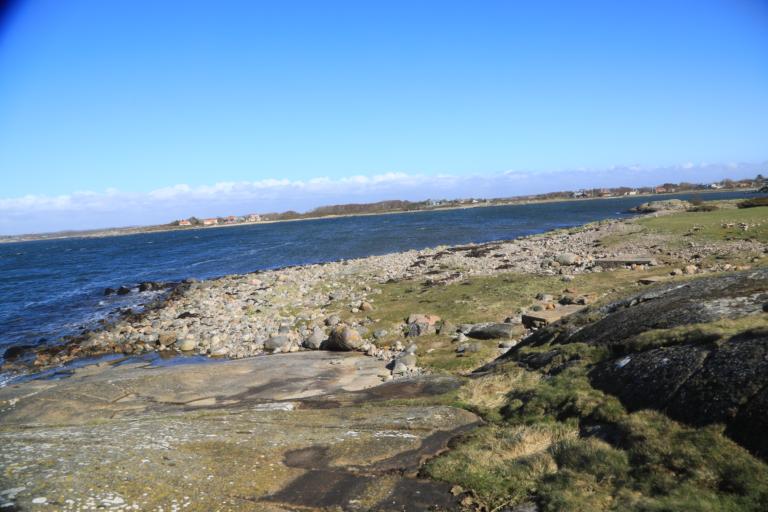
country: SE
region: Halland
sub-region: Varbergs Kommun
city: Varberg
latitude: 57.1229
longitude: 12.1939
